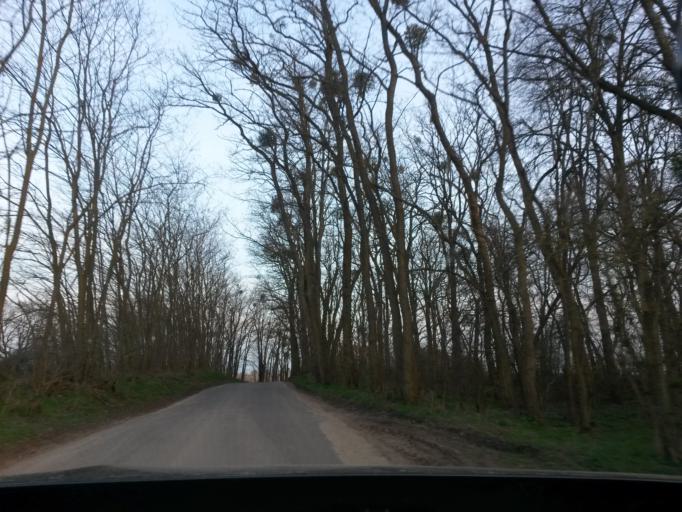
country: DE
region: Brandenburg
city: Protzel
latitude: 52.5761
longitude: 13.9628
